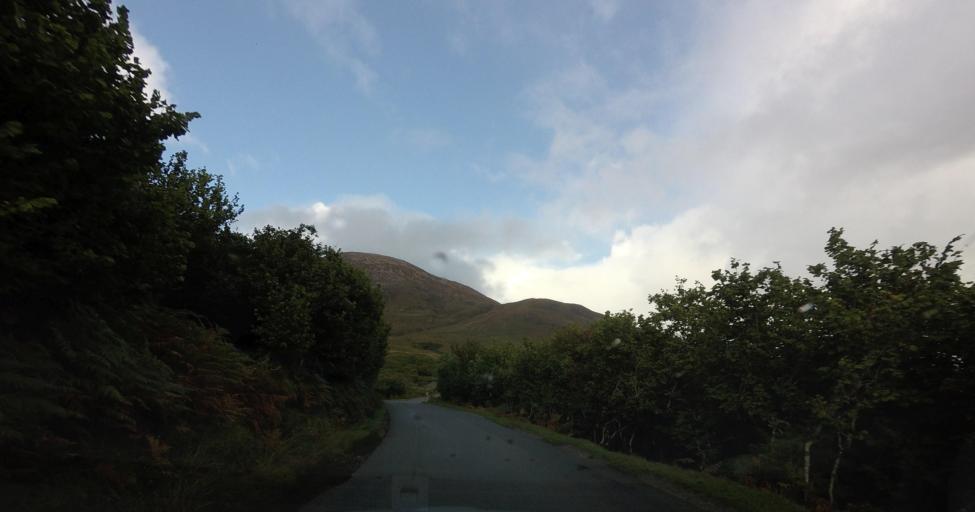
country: GB
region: Scotland
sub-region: Highland
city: Portree
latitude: 57.2107
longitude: -6.0017
